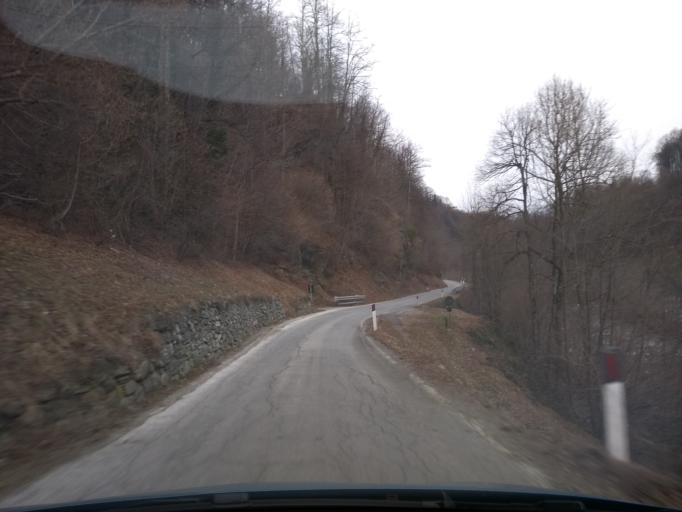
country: IT
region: Piedmont
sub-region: Provincia di Torino
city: Viu
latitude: 45.2321
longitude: 7.3539
